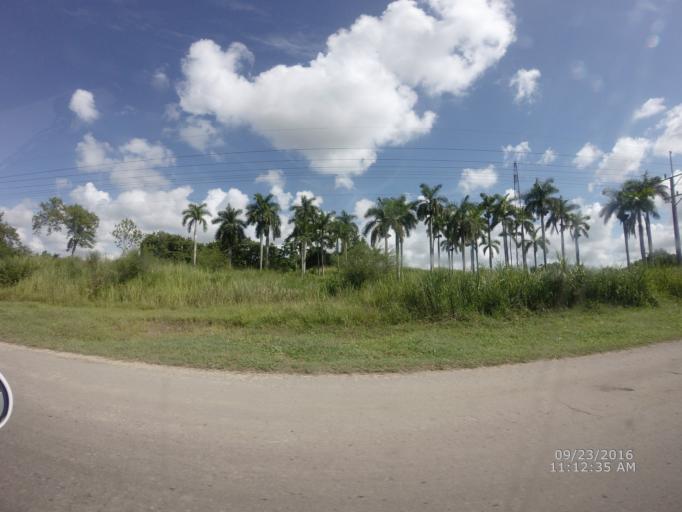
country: CU
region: La Habana
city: Arroyo Naranjo
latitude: 23.0301
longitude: -82.2859
